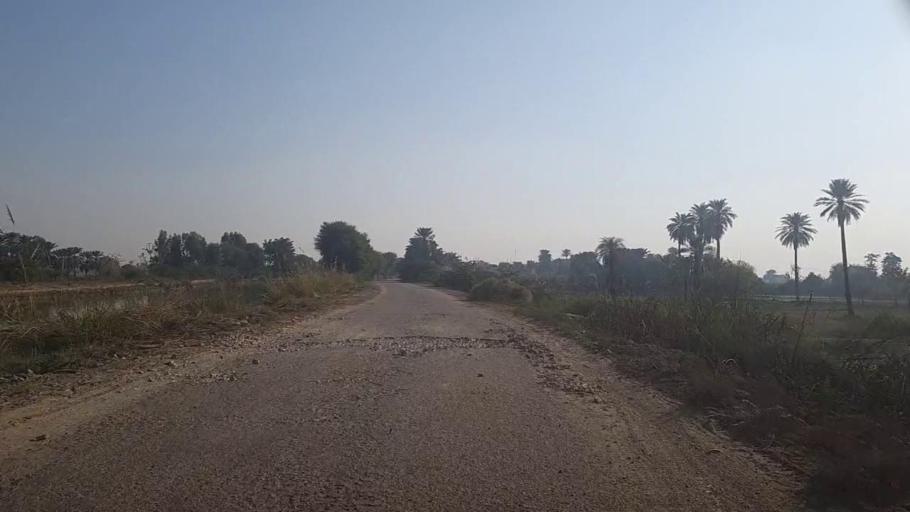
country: PK
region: Sindh
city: Bozdar
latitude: 27.2589
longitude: 68.6758
